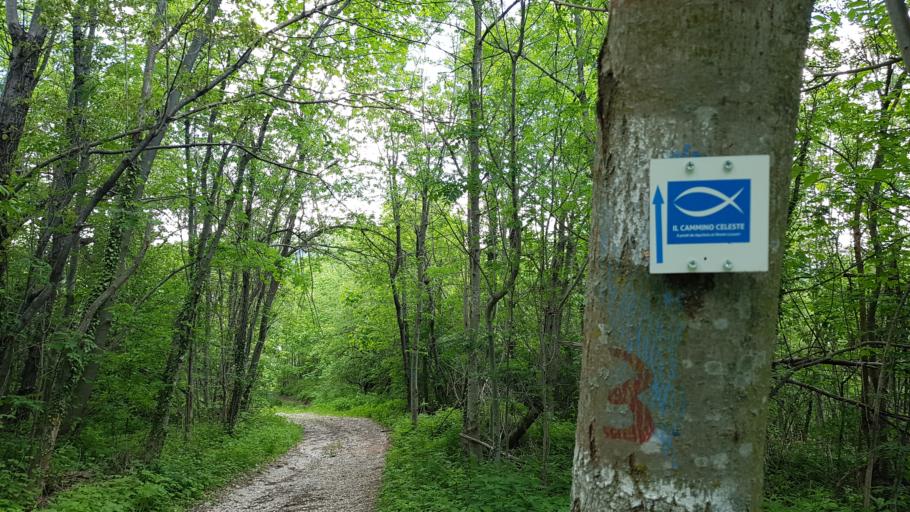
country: IT
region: Friuli Venezia Giulia
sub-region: Provincia di Udine
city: Pulfero
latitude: 46.1928
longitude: 13.4259
